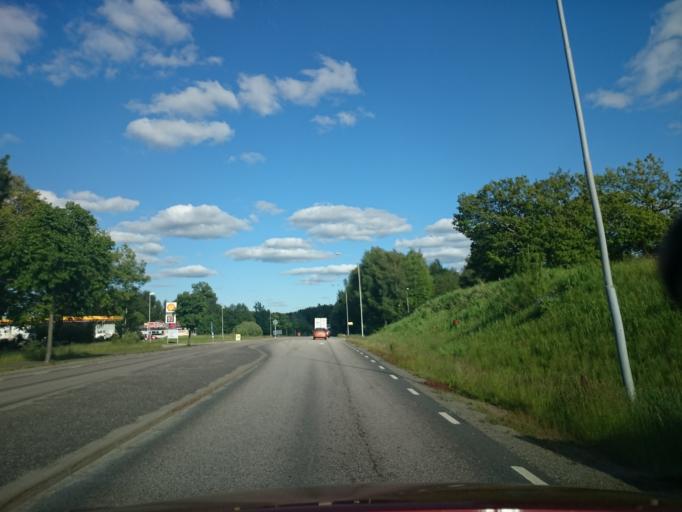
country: SE
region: Vaestra Goetaland
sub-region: Harryda Kommun
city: Molnlycke
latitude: 57.6687
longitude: 12.0944
